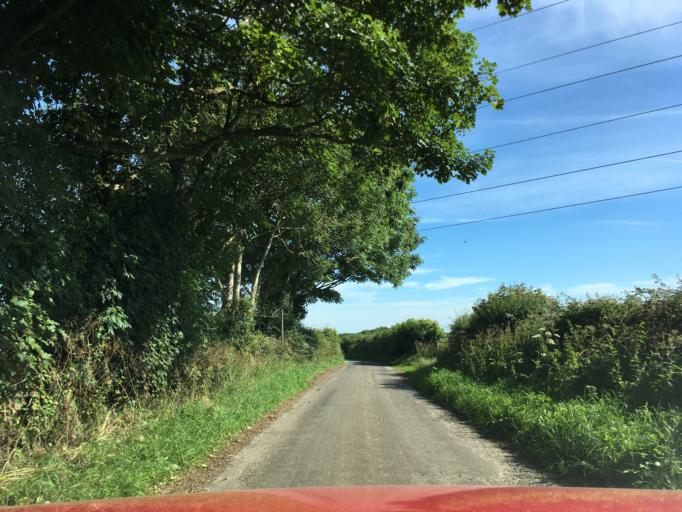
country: GB
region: England
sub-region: Wiltshire
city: Nettleton
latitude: 51.4793
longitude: -2.2645
